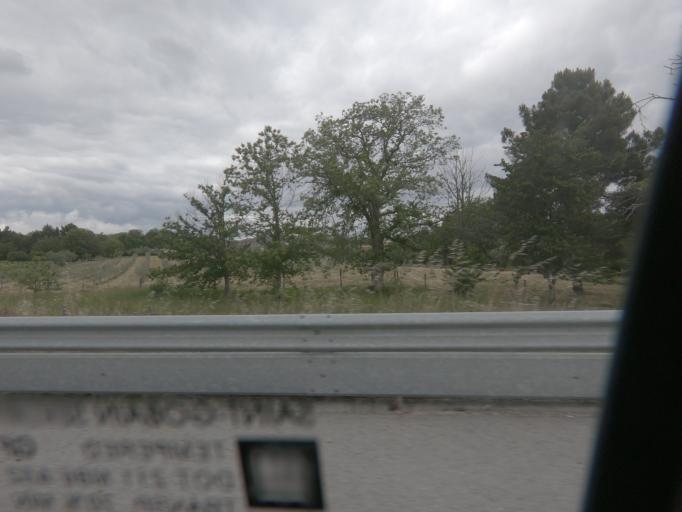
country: PT
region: Vila Real
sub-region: Sabrosa
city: Vilela
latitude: 41.2665
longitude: -7.6373
